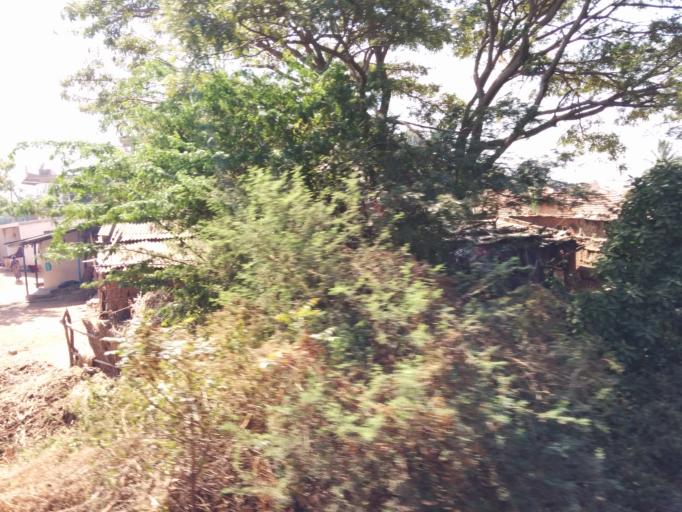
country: IN
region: Karnataka
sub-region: Dharwad
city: Hubli
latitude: 15.3868
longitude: 75.1184
